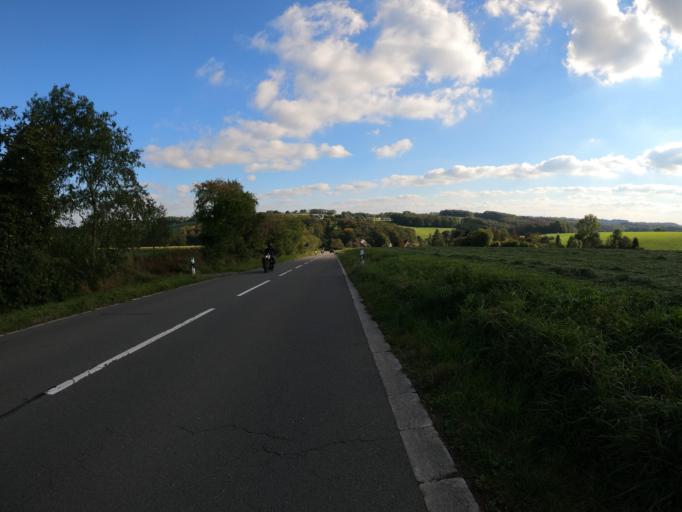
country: DE
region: North Rhine-Westphalia
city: Radevormwald
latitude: 51.2286
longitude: 7.3415
